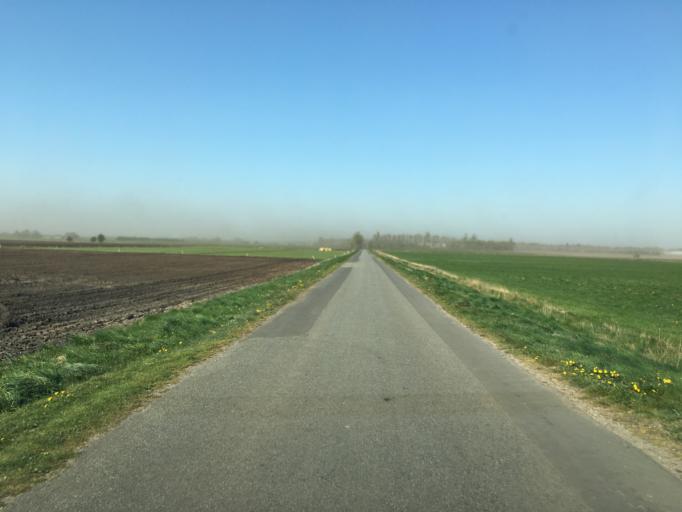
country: DK
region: South Denmark
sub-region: Tonder Kommune
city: Logumkloster
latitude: 55.0528
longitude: 9.0455
